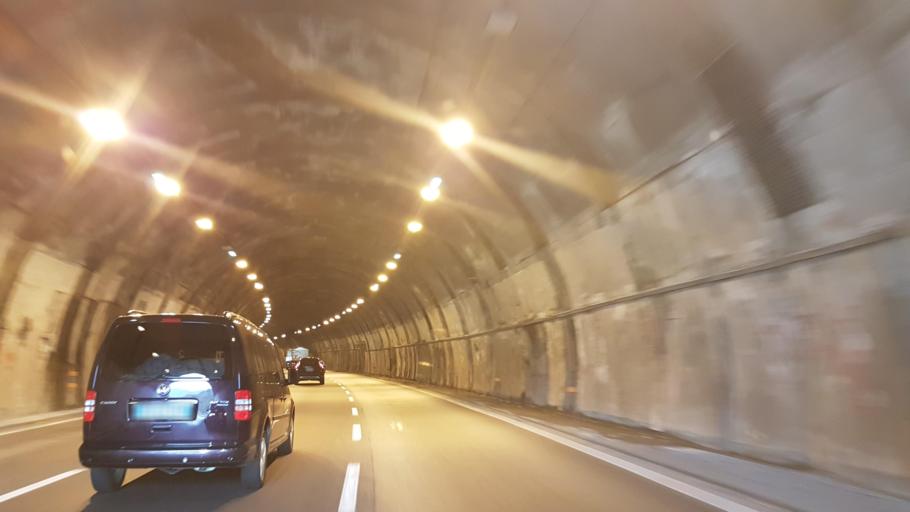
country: IT
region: Liguria
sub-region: Provincia di Genova
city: Masone
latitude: 44.4958
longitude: 8.7285
